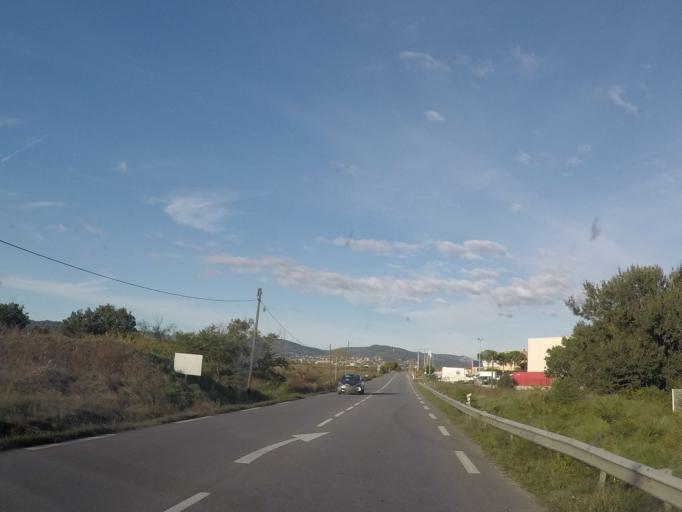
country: FR
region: Provence-Alpes-Cote d'Azur
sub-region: Departement des Alpes-de-Haute-Provence
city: Sainte-Tulle
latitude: 43.7961
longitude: 5.7758
